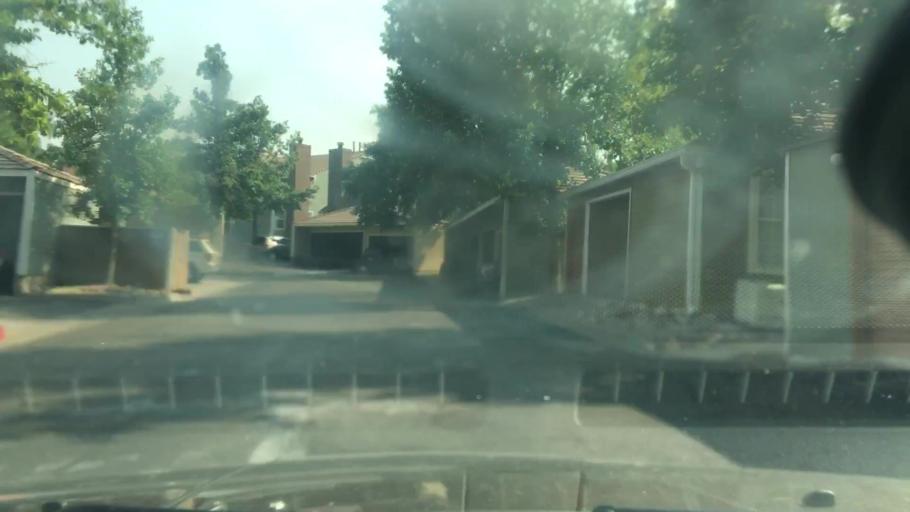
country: US
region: Colorado
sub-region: Douglas County
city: Acres Green
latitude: 39.5677
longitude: -104.9087
